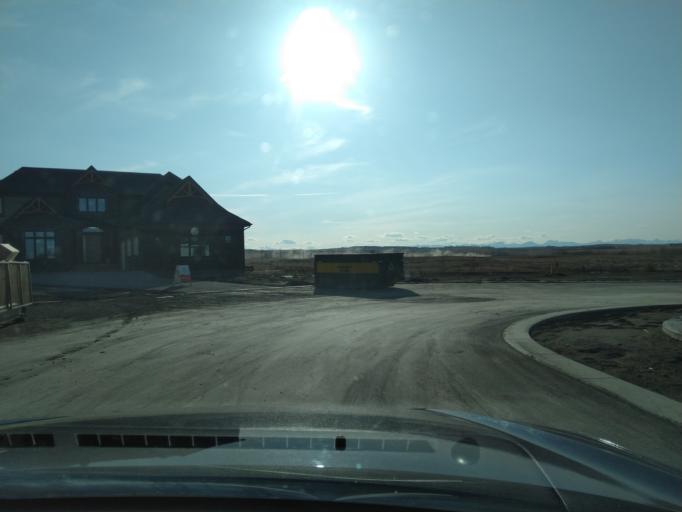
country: CA
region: Alberta
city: Cochrane
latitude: 51.1113
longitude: -114.4082
